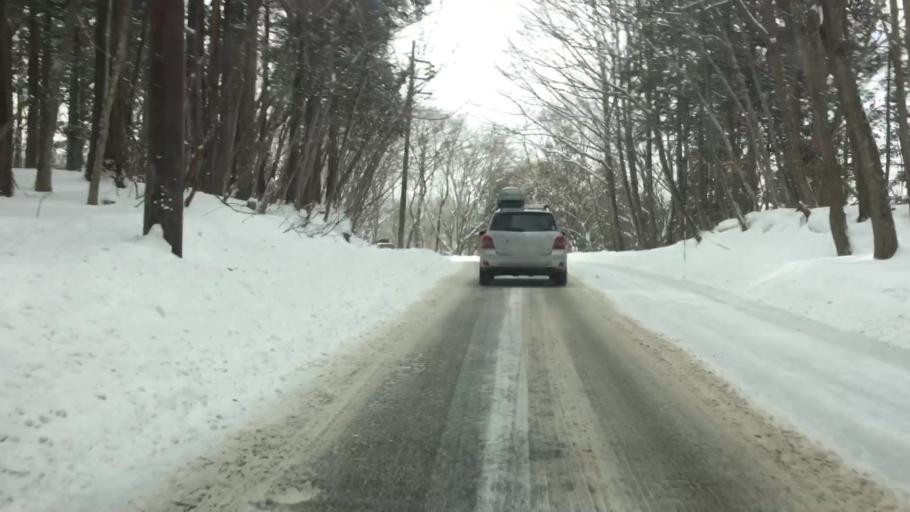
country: JP
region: Tochigi
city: Yaita
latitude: 36.9480
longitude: 139.7570
